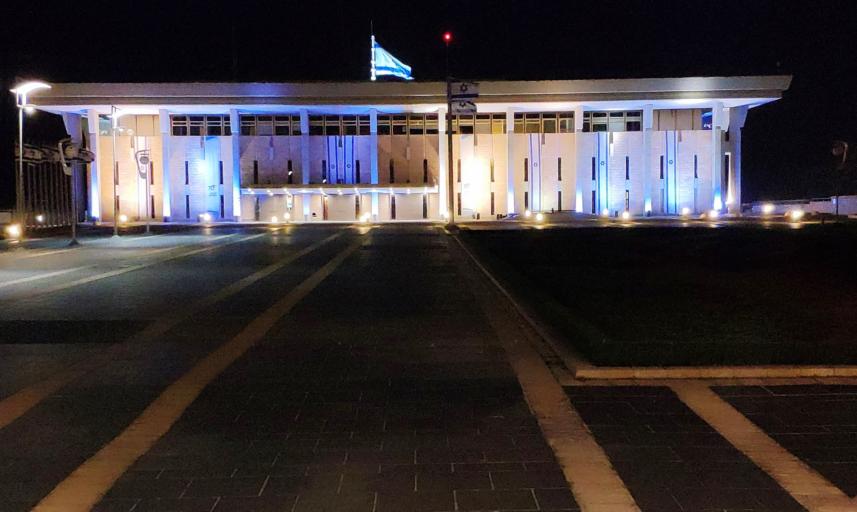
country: IL
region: Jerusalem
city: Jerusalem
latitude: 31.7779
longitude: 35.2049
